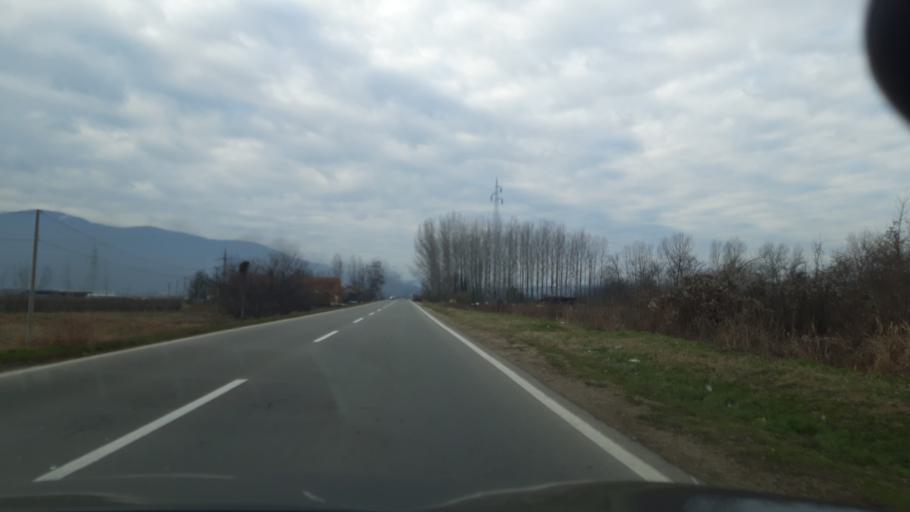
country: RS
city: Lipnicki Sor
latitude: 44.5465
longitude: 19.1928
